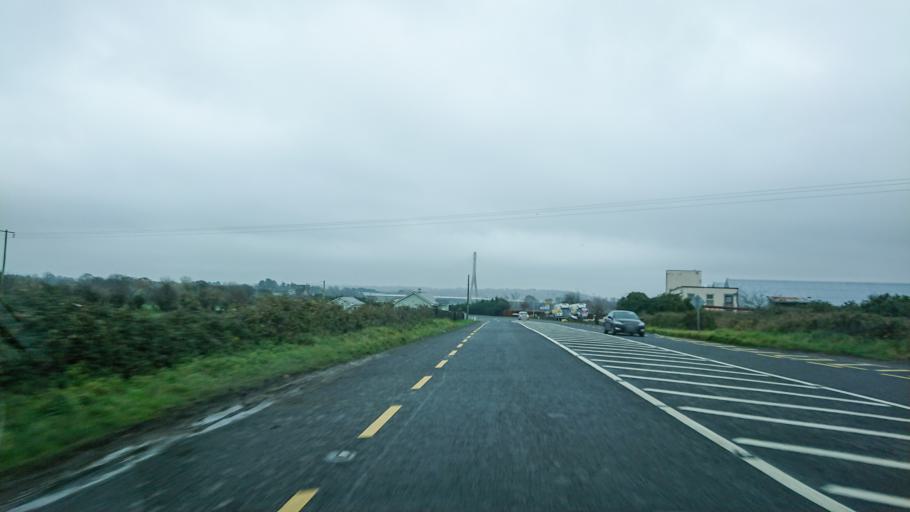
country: IE
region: Munster
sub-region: Waterford
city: Waterford
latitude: 52.2807
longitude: -7.1695
